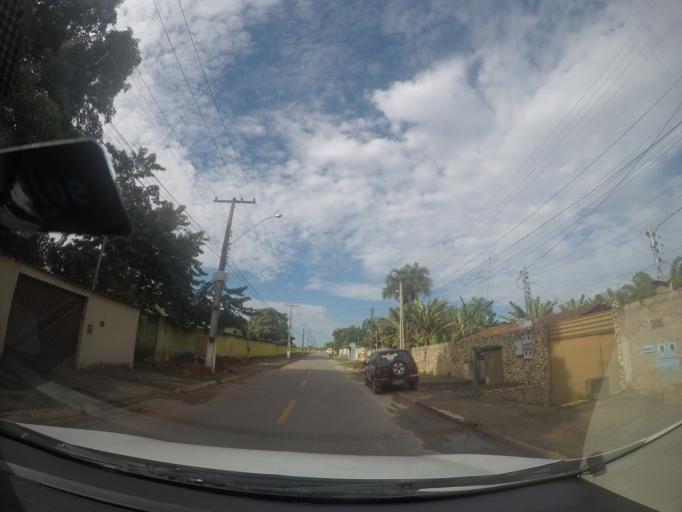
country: BR
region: Goias
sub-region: Goiania
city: Goiania
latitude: -16.6878
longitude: -49.1889
